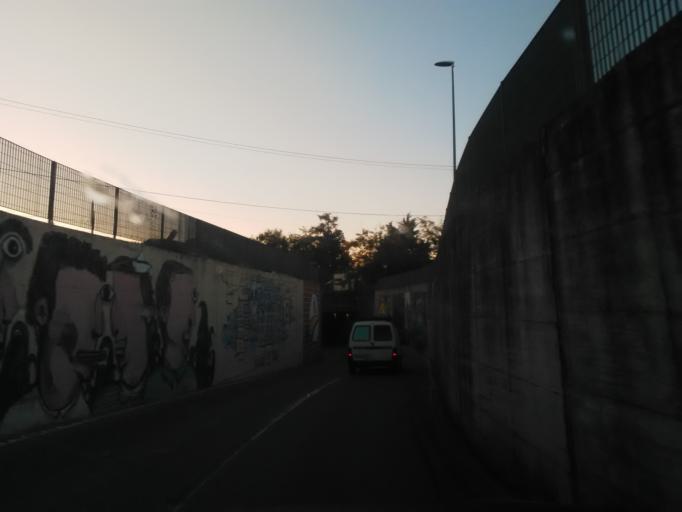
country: IT
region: Piedmont
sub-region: Provincia di Vercelli
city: Tronzano Vercellese
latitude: 45.3438
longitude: 8.1682
